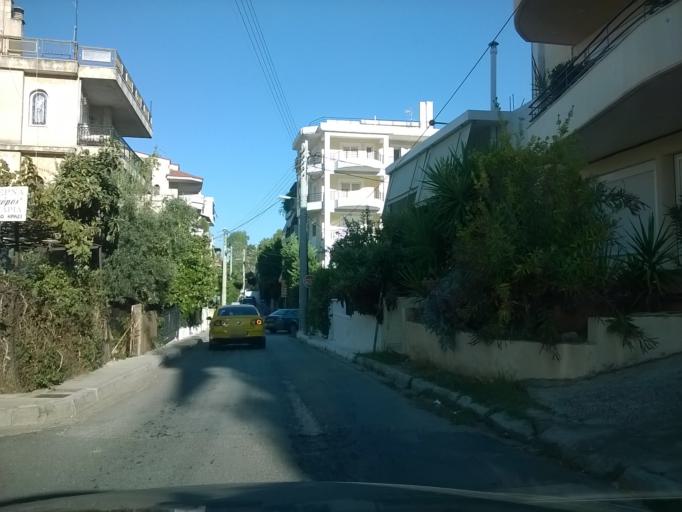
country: GR
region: Attica
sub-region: Nomarchia Athinas
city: Cholargos
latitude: 37.9974
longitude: 23.8104
